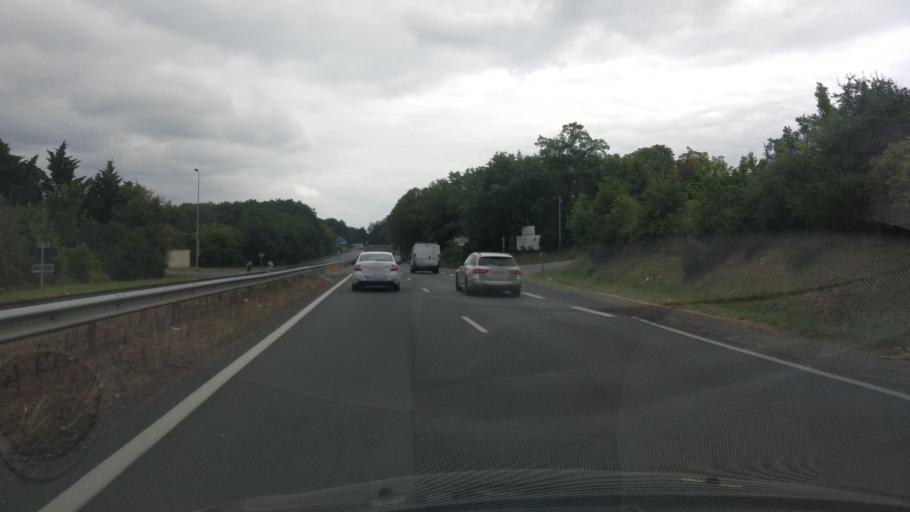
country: FR
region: Poitou-Charentes
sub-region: Departement de la Vienne
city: Biard
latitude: 46.5526
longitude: 0.3134
